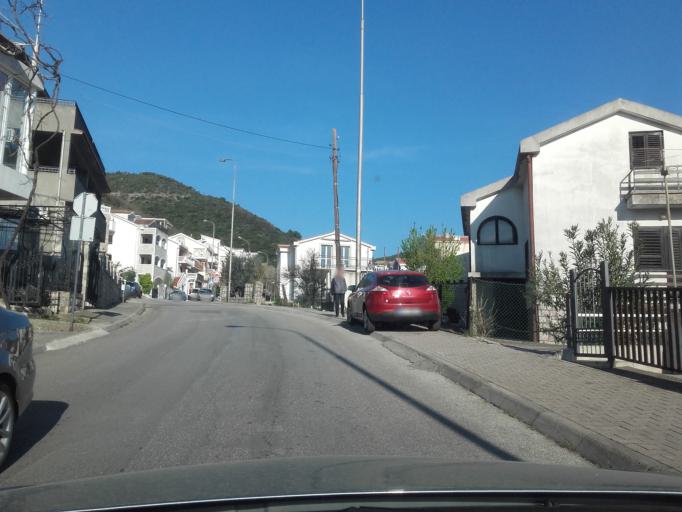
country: ME
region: Budva
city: Budva
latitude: 42.2873
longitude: 18.8335
